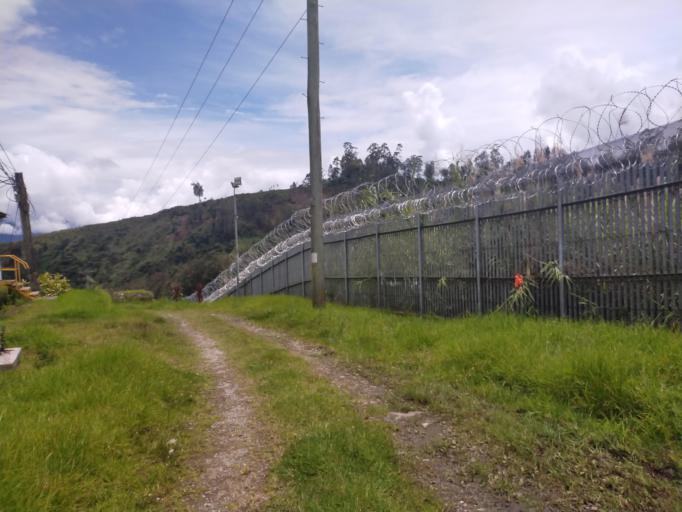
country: PG
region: Enga
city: Porgera
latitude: -5.4613
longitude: 143.1053
